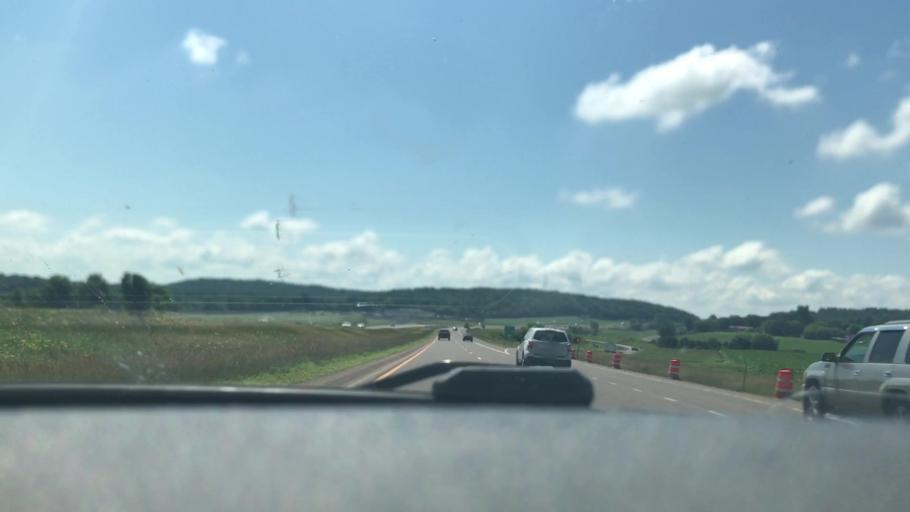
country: US
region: Wisconsin
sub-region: Chippewa County
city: Chippewa Falls
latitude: 44.9702
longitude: -91.4309
